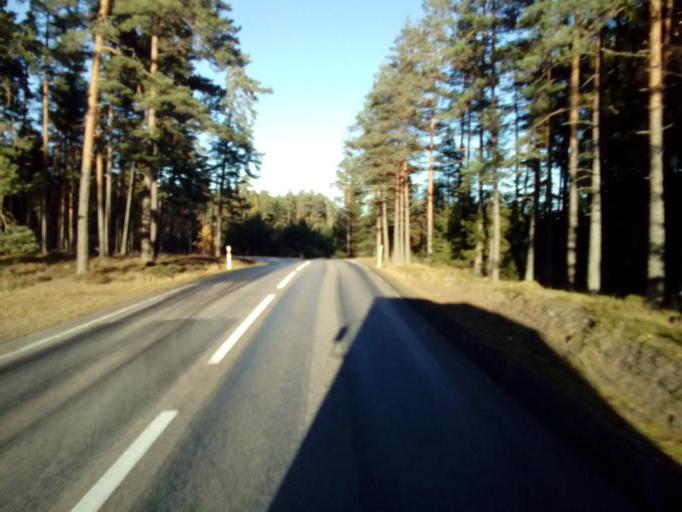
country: SE
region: OErebro
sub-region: Hallsbergs Kommun
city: Palsboda
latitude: 58.8832
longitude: 15.4236
